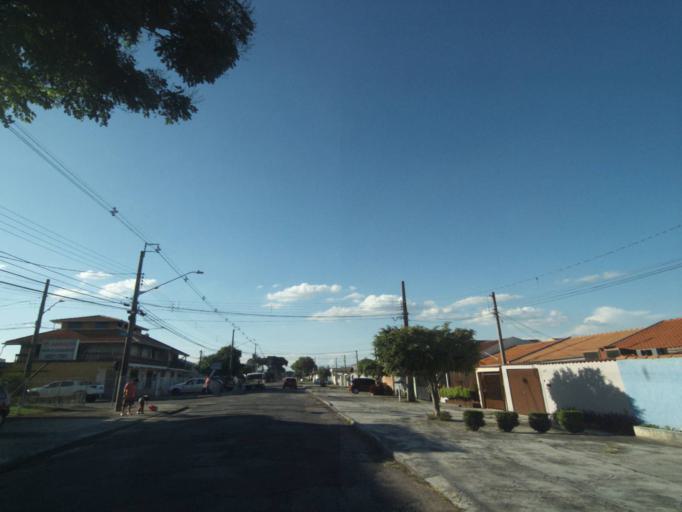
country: BR
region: Parana
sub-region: Pinhais
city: Pinhais
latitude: -25.4607
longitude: -49.2029
